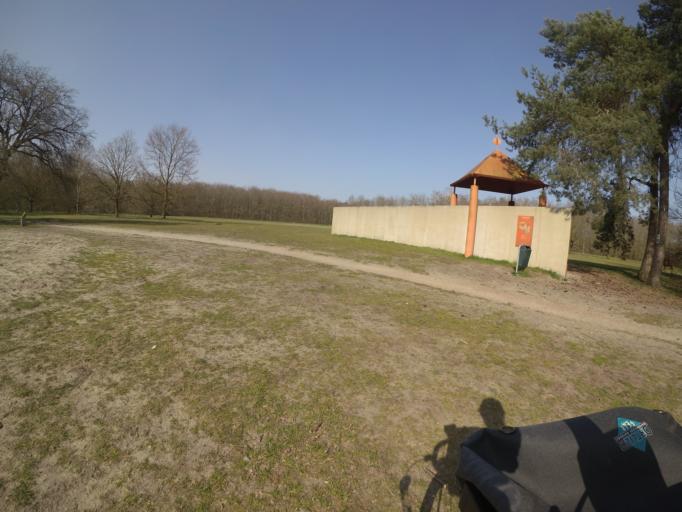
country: NL
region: North Brabant
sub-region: Gemeente Maasdonk
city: Geffen
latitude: 51.6924
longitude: 5.4401
